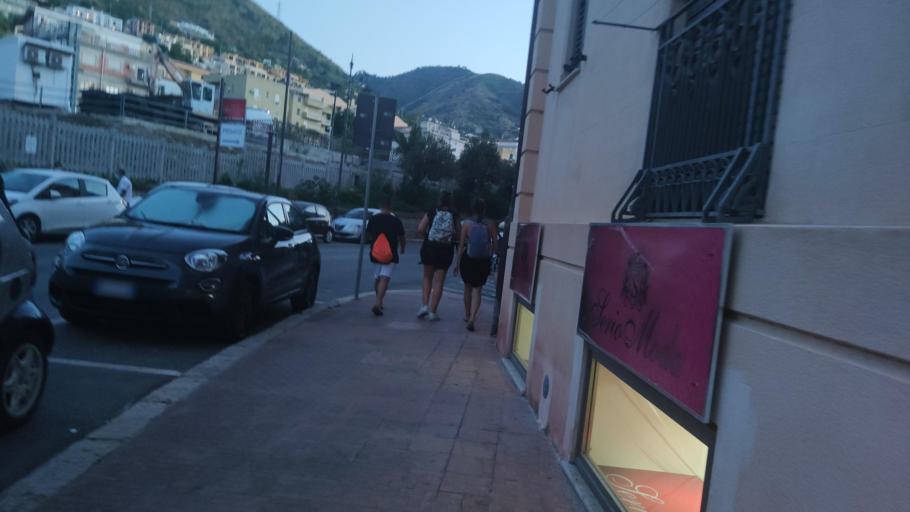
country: IT
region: Sicily
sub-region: Palermo
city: Cefalu
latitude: 38.0339
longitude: 14.0211
